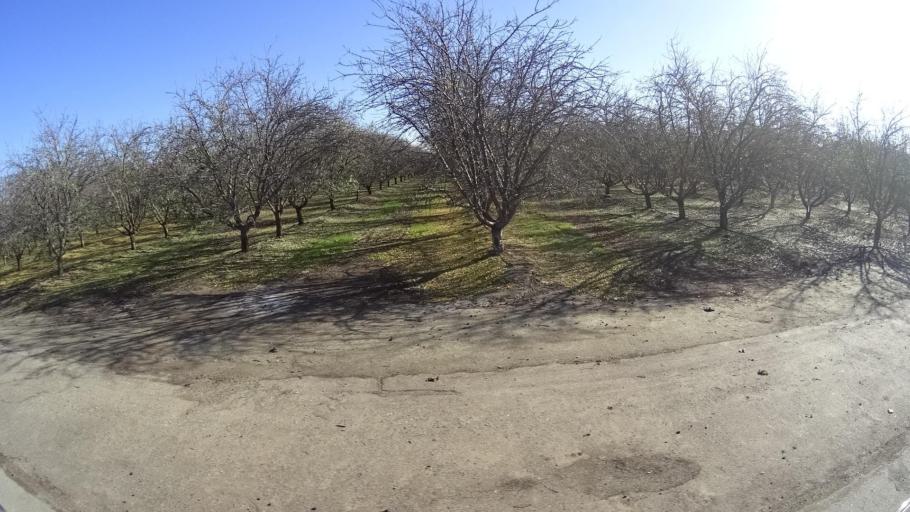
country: US
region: California
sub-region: Kern County
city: Delano
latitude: 35.7266
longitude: -119.2852
